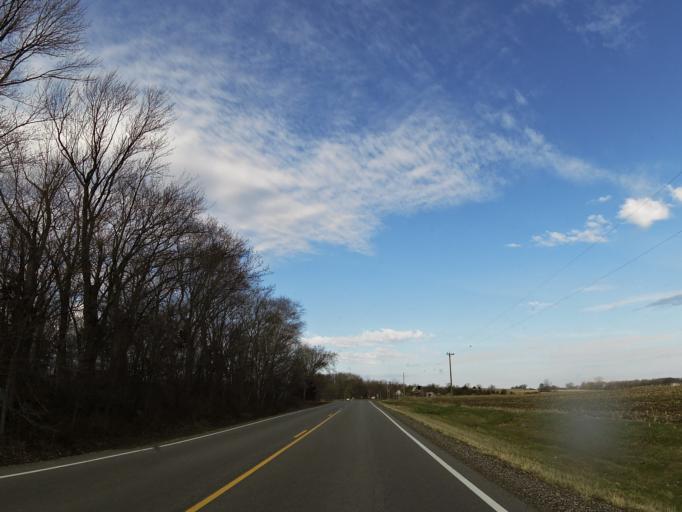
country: US
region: Minnesota
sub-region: Dakota County
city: Hastings
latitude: 44.8189
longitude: -92.8569
